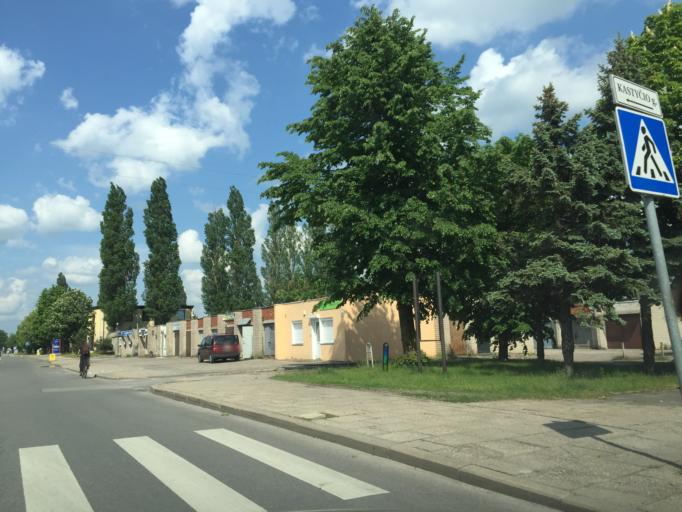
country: LT
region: Klaipedos apskritis
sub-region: Klaipeda
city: Palanga
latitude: 55.9223
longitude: 21.0738
